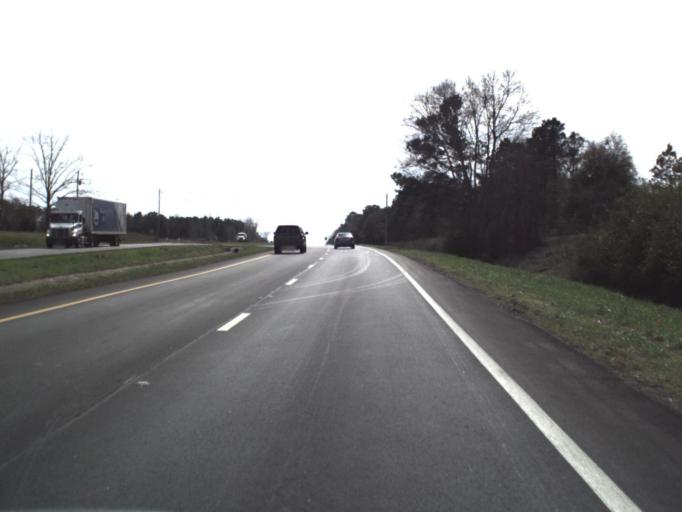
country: US
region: Florida
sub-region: Washington County
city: Chipley
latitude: 30.6881
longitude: -85.3930
